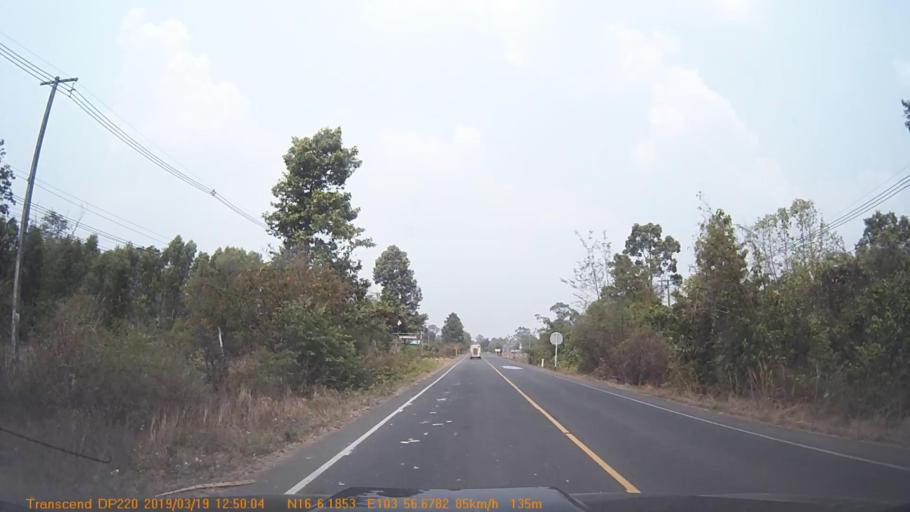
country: TH
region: Roi Et
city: Selaphum
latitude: 16.1036
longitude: 103.9447
